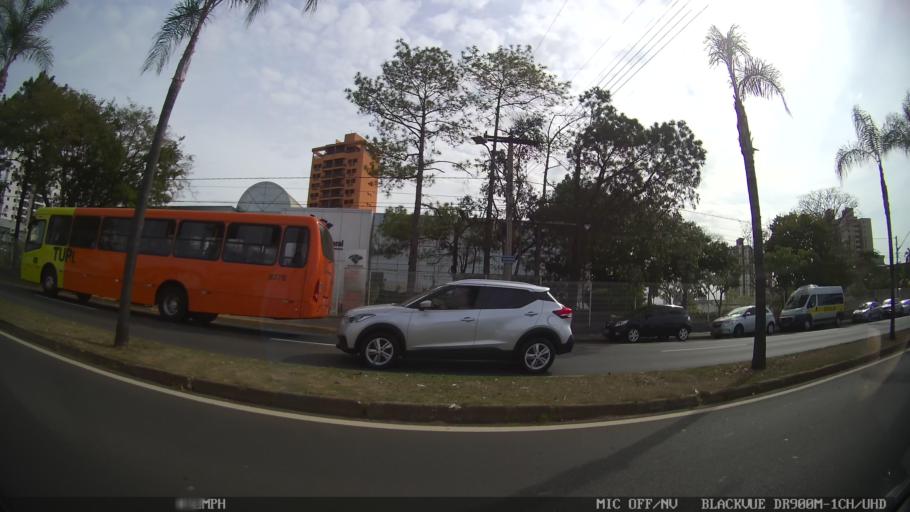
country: BR
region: Sao Paulo
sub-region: Piracicaba
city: Piracicaba
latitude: -22.7185
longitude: -47.6330
